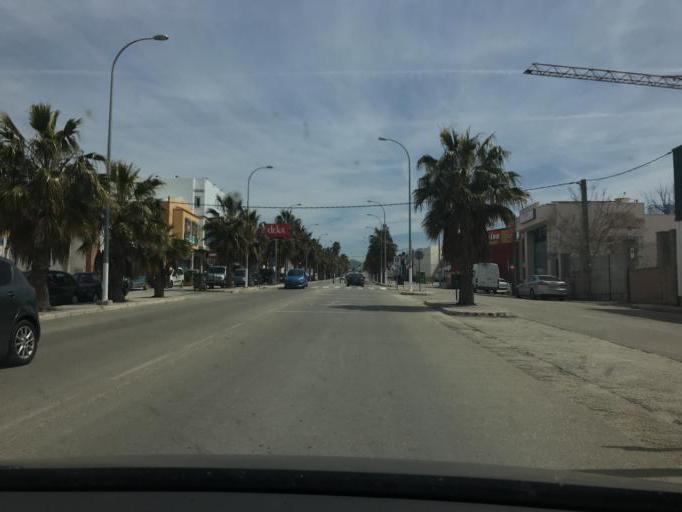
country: ES
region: Andalusia
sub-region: Provincia de Jaen
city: Torredonjimeno
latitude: 37.7631
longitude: -3.9419
